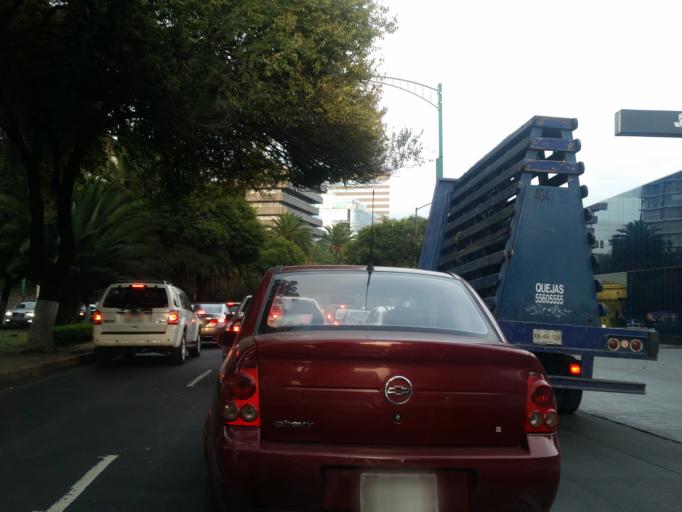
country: MX
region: Mexico City
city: Miguel Hidalgo
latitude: 19.4293
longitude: -99.2153
